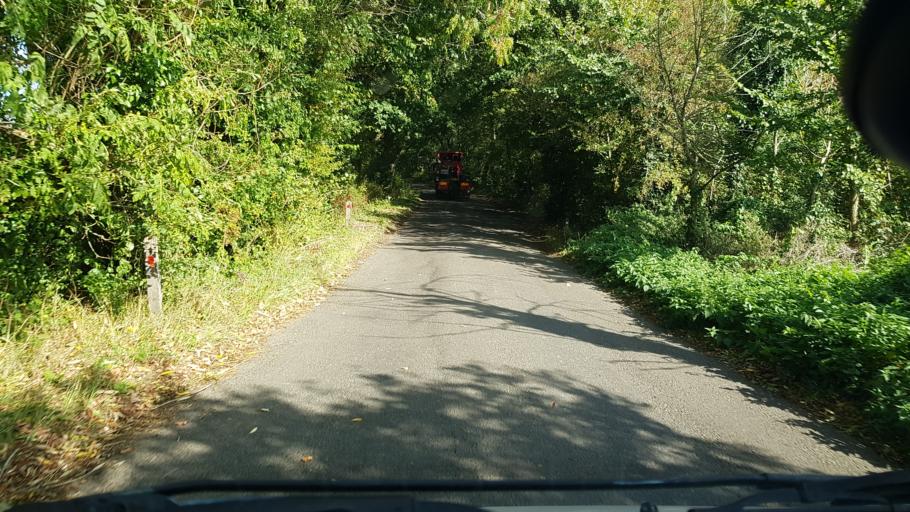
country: GB
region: England
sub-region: Surrey
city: Shalford
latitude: 51.2099
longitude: -0.5964
